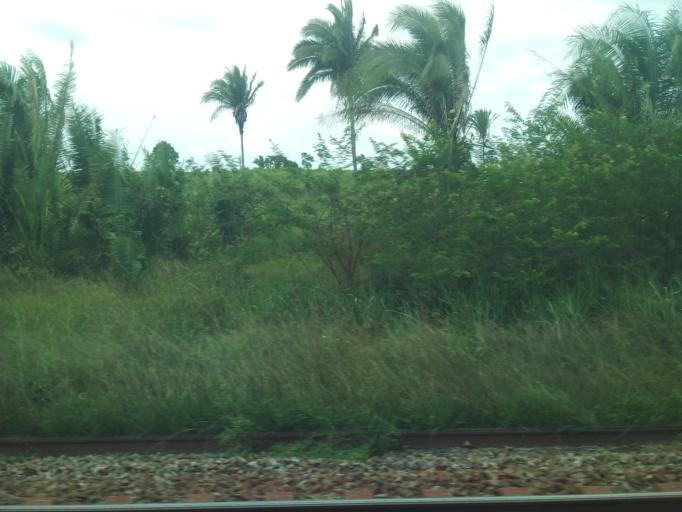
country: BR
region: Maranhao
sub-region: Santa Ines
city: Santa Ines
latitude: -3.6837
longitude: -45.3424
